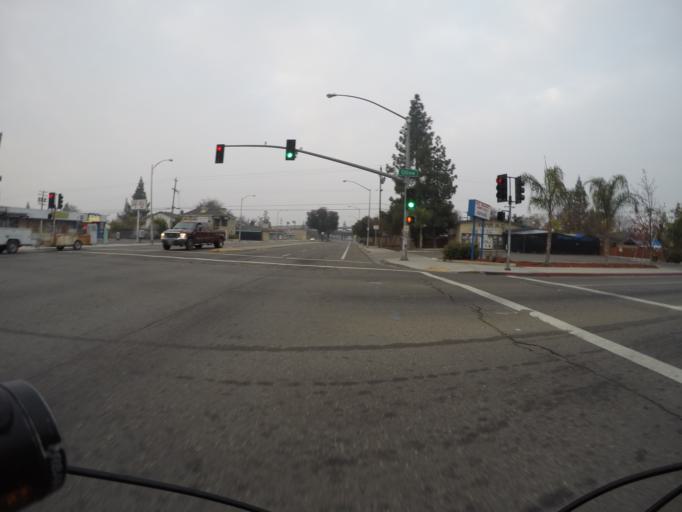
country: US
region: California
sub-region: Fresno County
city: Fresno
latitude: 36.7577
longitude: -119.7727
